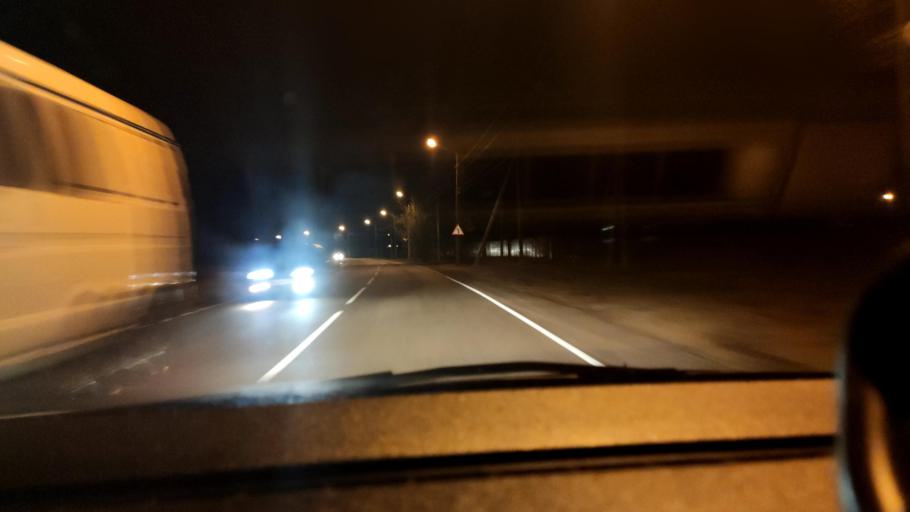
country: RU
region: Voronezj
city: Shilovo
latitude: 51.5500
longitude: 39.0812
